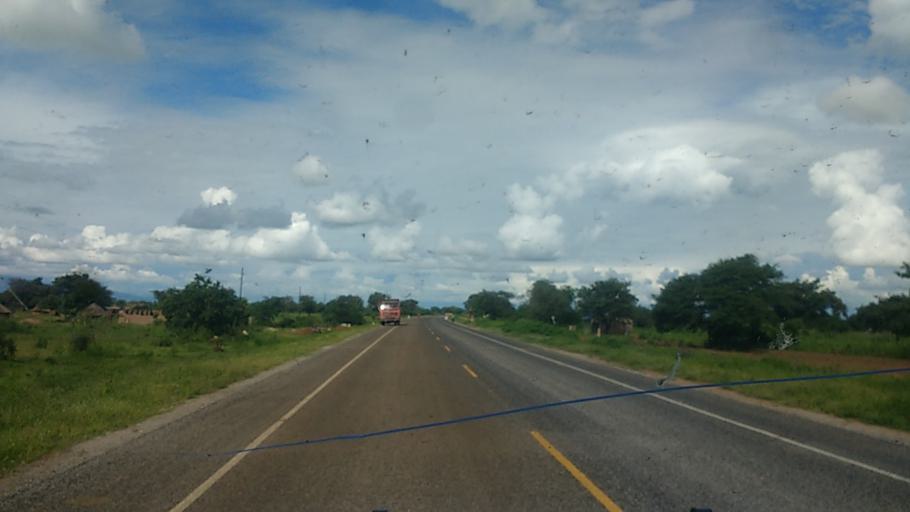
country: UG
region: Eastern Region
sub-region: Katakwi District
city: Katakwi
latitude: 1.9203
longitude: 33.9954
